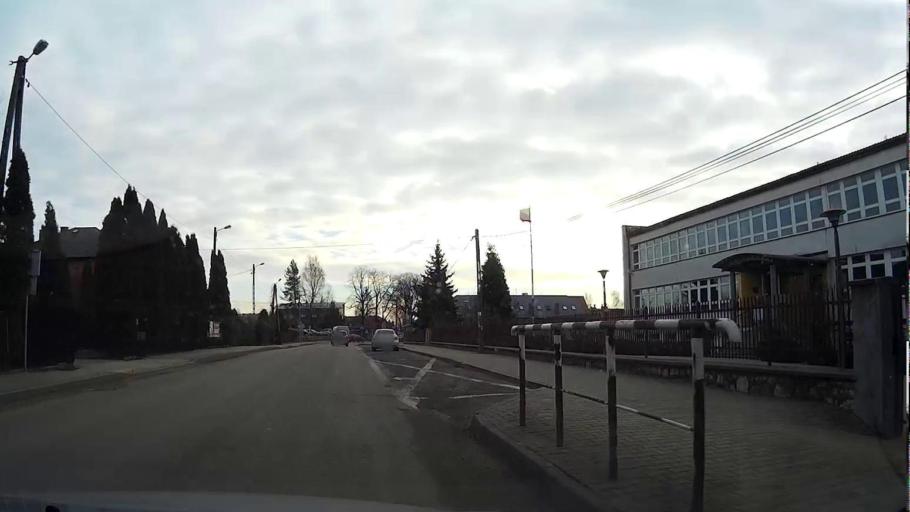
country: PL
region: Lesser Poland Voivodeship
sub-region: Powiat chrzanowski
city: Alwernia
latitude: 50.0650
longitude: 19.5432
